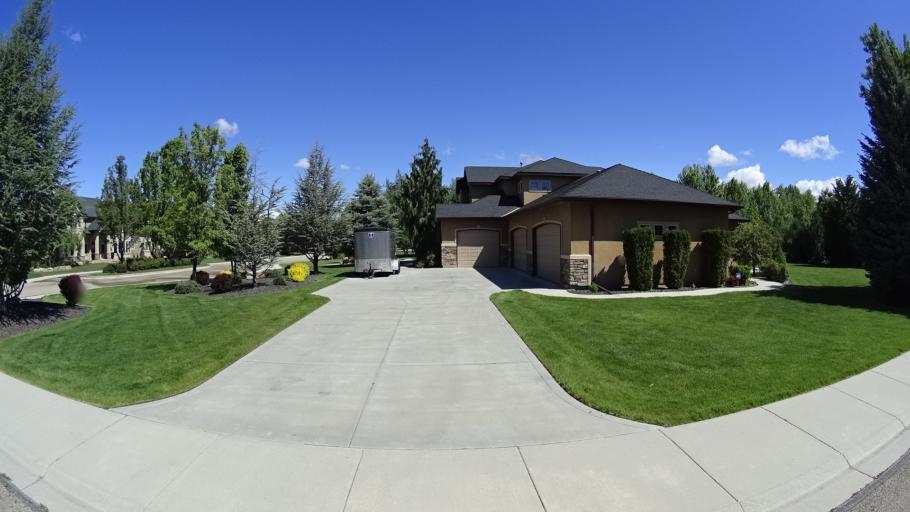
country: US
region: Idaho
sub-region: Ada County
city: Eagle
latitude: 43.6682
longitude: -116.3831
